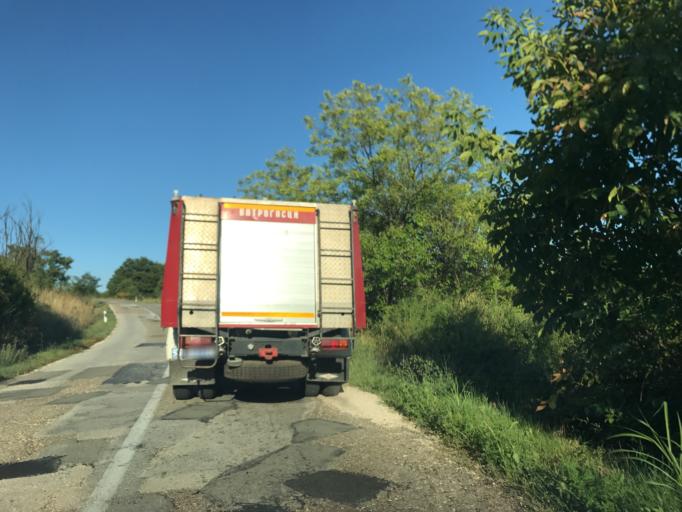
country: RS
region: Central Serbia
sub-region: Borski Okrug
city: Negotin
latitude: 44.2320
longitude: 22.4438
